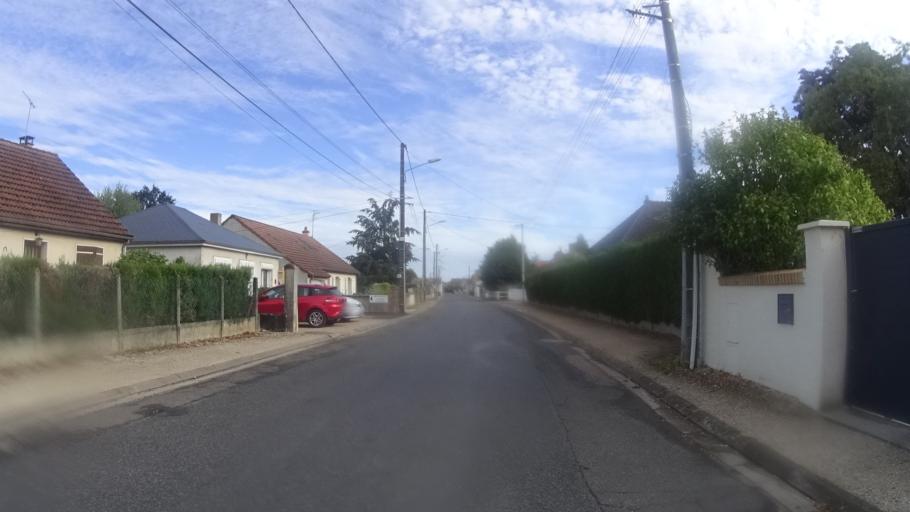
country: FR
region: Centre
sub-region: Departement du Loiret
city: Chateauneuf-sur-Loire
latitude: 47.8716
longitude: 2.2167
